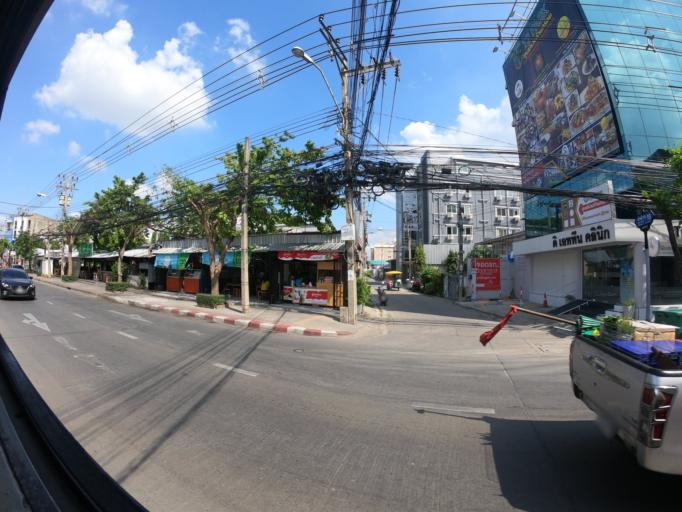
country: TH
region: Bangkok
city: Lat Phrao
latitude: 13.8071
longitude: 100.6086
